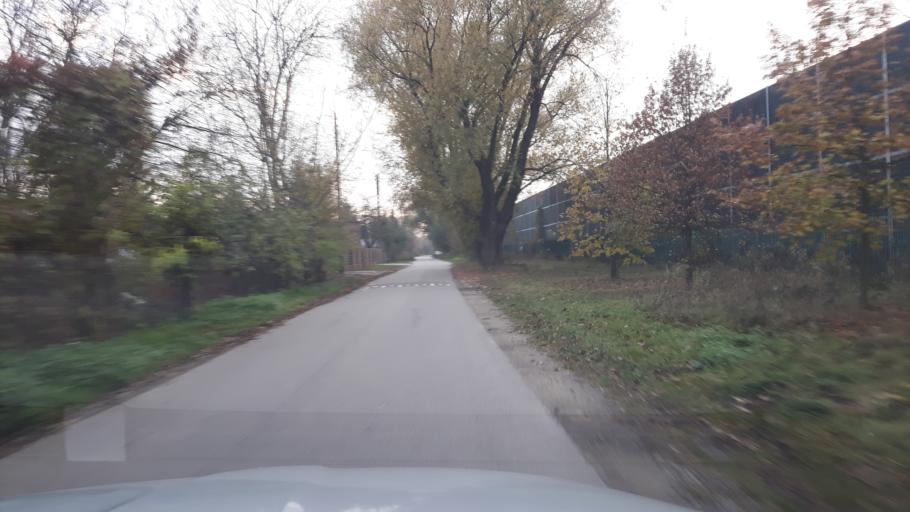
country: PL
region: Masovian Voivodeship
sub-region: Warszawa
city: Wilanow
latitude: 52.1885
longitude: 21.0962
